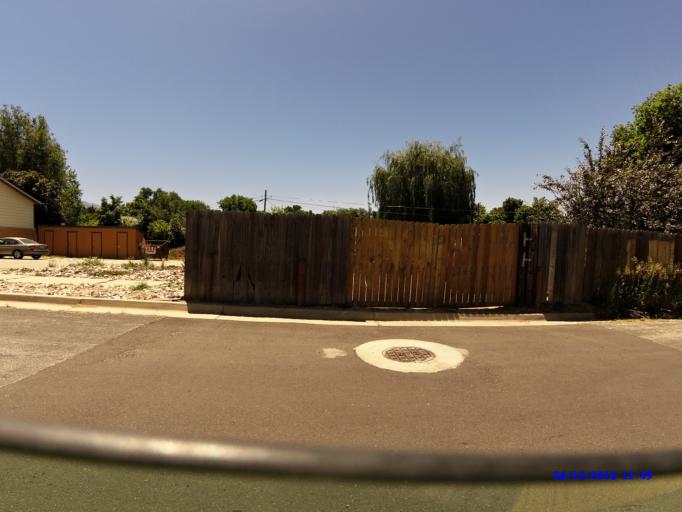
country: US
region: Utah
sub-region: Weber County
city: South Ogden
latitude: 41.2068
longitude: -111.9526
